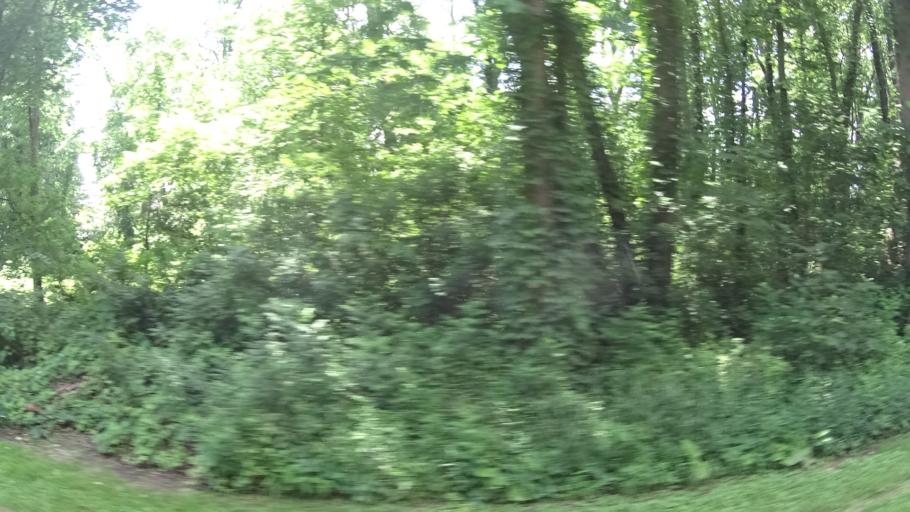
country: US
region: Ohio
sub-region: Erie County
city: Milan
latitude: 41.3227
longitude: -82.5434
